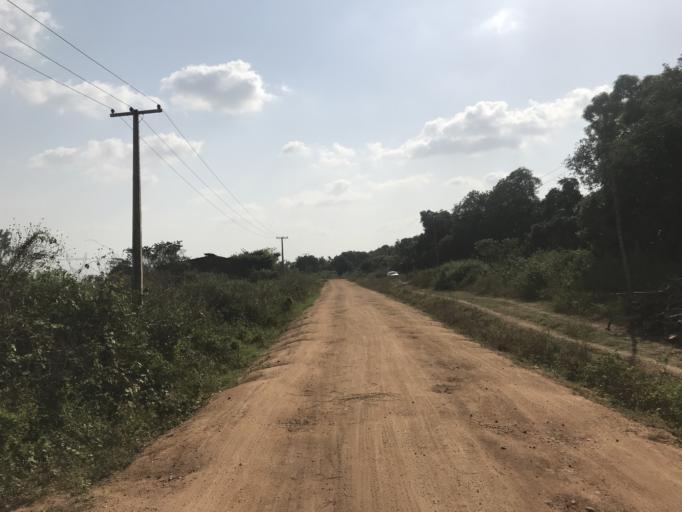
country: NG
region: Osun
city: Osogbo
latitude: 7.8415
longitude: 4.5731
